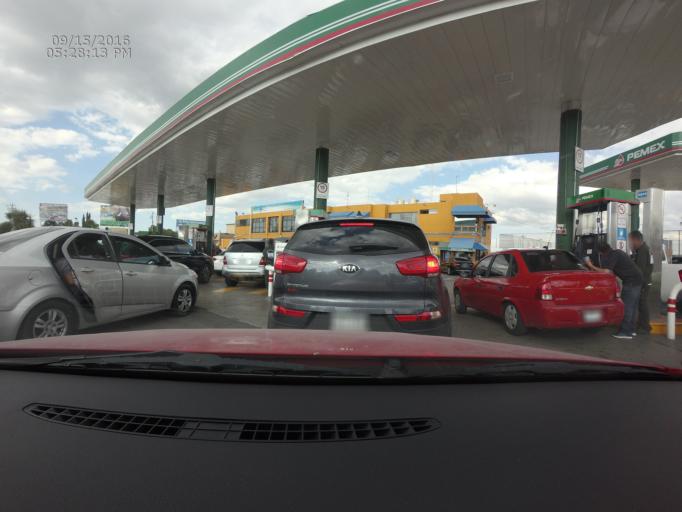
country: MX
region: Mexico
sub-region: Cuautitlan
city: Barrio Tlatenco
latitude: 19.7400
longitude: -99.2113
